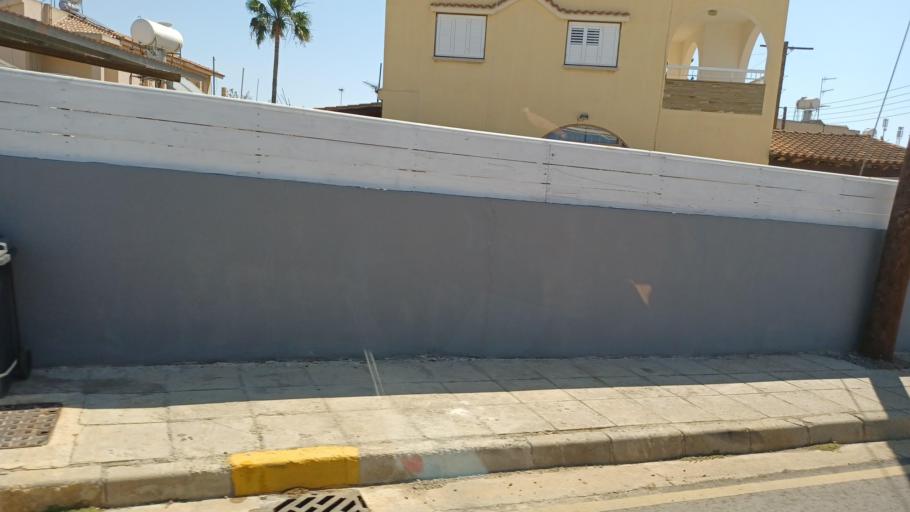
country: CY
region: Ammochostos
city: Liopetri
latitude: 35.0103
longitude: 33.8914
